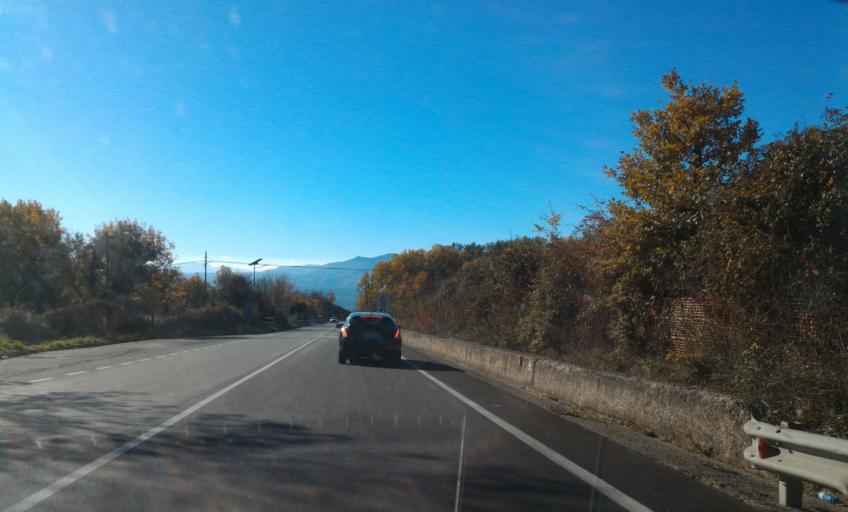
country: IT
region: Calabria
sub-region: Provincia di Cosenza
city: Rovito
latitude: 39.3078
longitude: 16.3247
